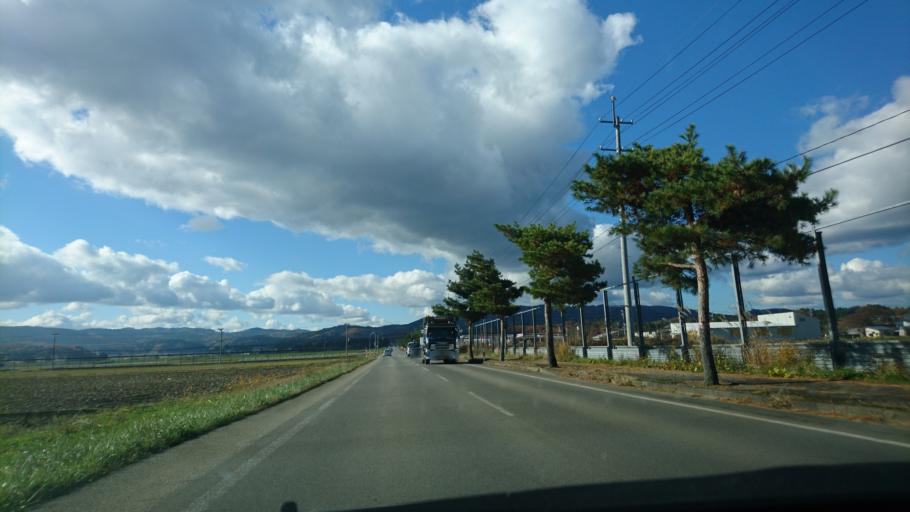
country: JP
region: Akita
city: Yuzawa
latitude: 39.2744
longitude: 140.4136
